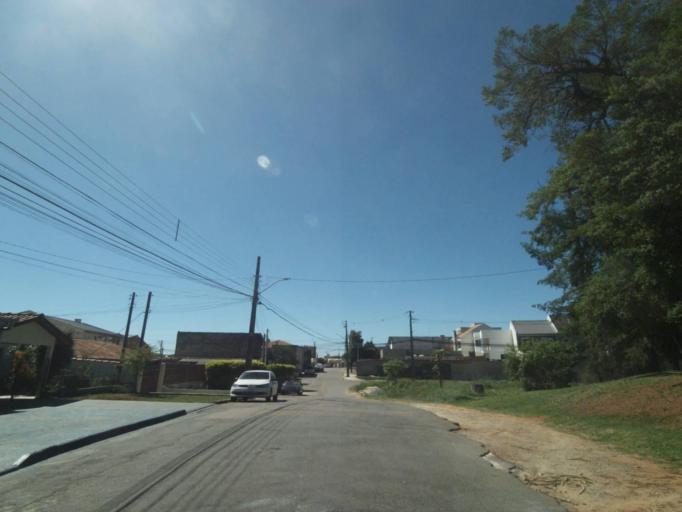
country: BR
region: Parana
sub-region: Curitiba
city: Curitiba
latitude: -25.4621
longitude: -49.3493
